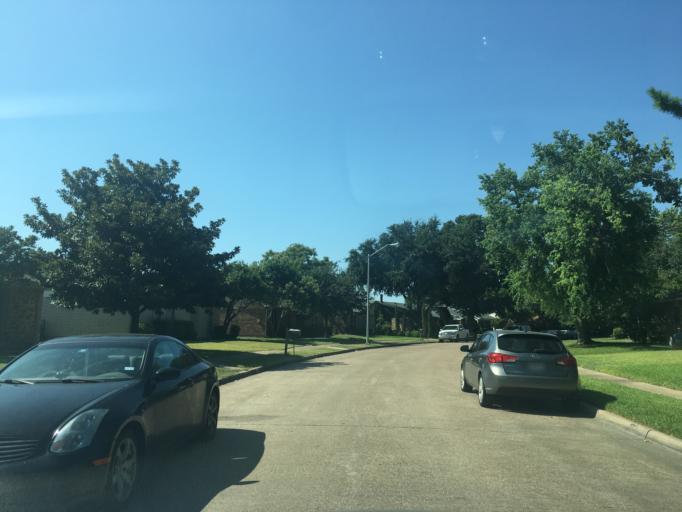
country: US
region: Texas
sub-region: Dallas County
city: Garland
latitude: 32.8560
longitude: -96.6579
